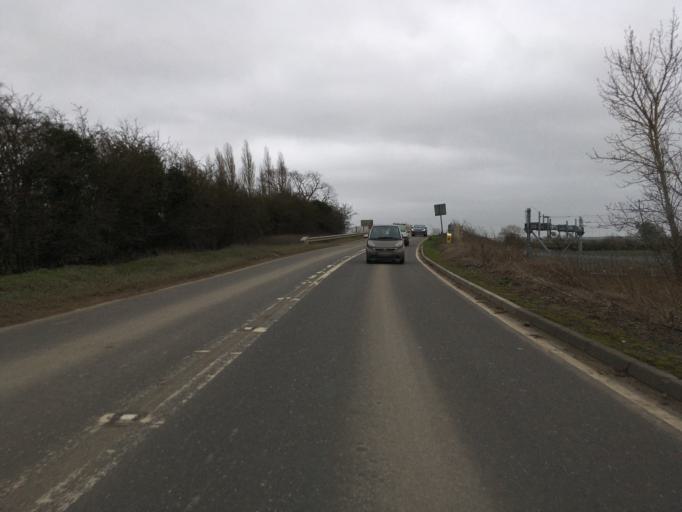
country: GB
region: England
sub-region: Oxfordshire
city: Stanford in the Vale
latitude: 51.6134
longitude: -1.4891
